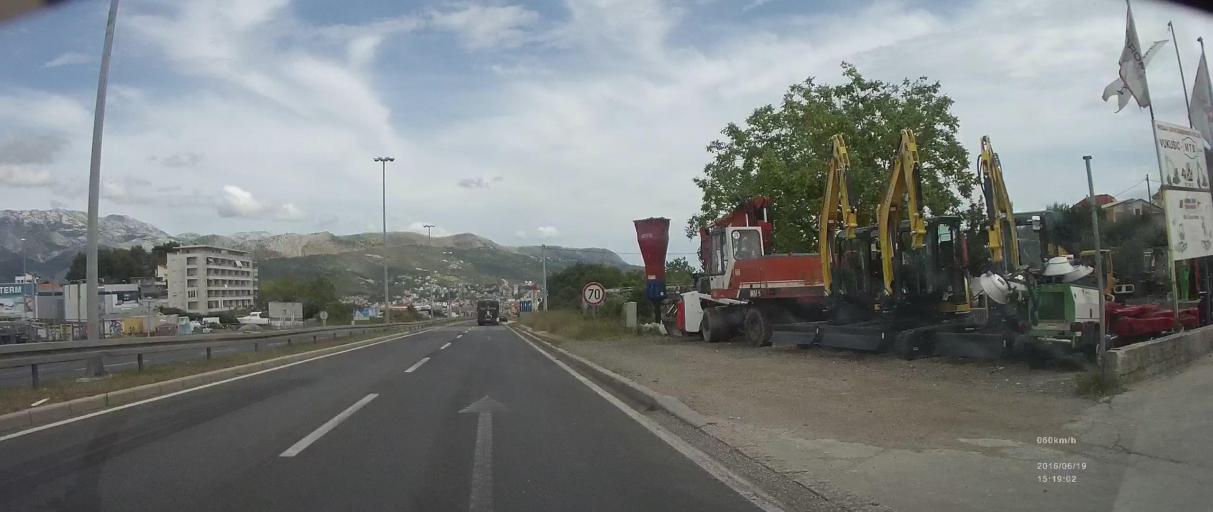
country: HR
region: Splitsko-Dalmatinska
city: Kamen
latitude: 43.5078
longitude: 16.5004
